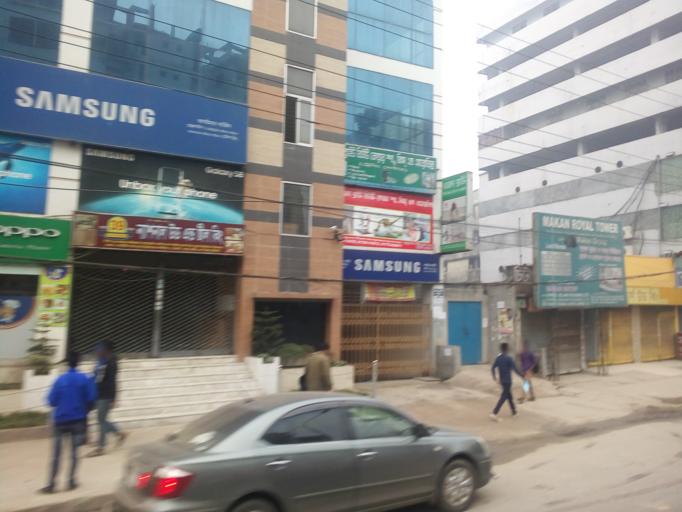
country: BD
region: Dhaka
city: Azimpur
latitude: 23.7891
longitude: 90.3760
